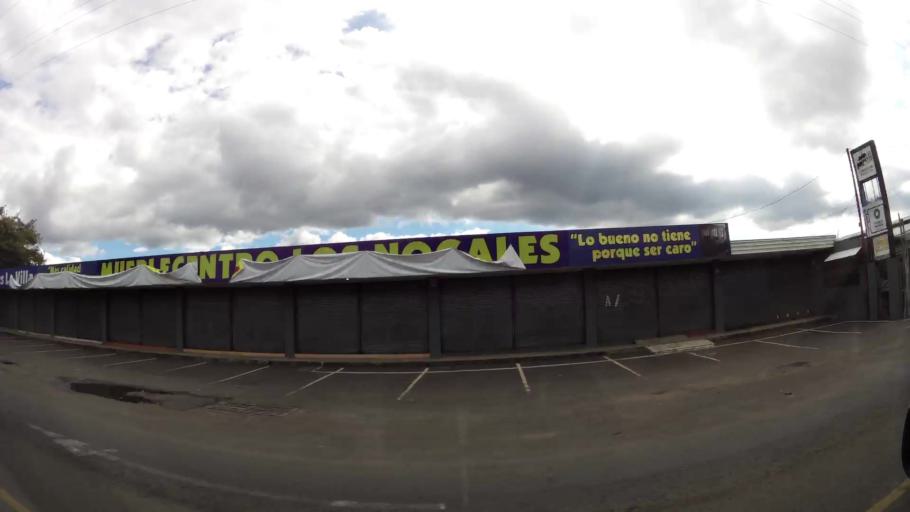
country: CR
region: San Jose
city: San Rafael
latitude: 9.9487
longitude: -84.1403
